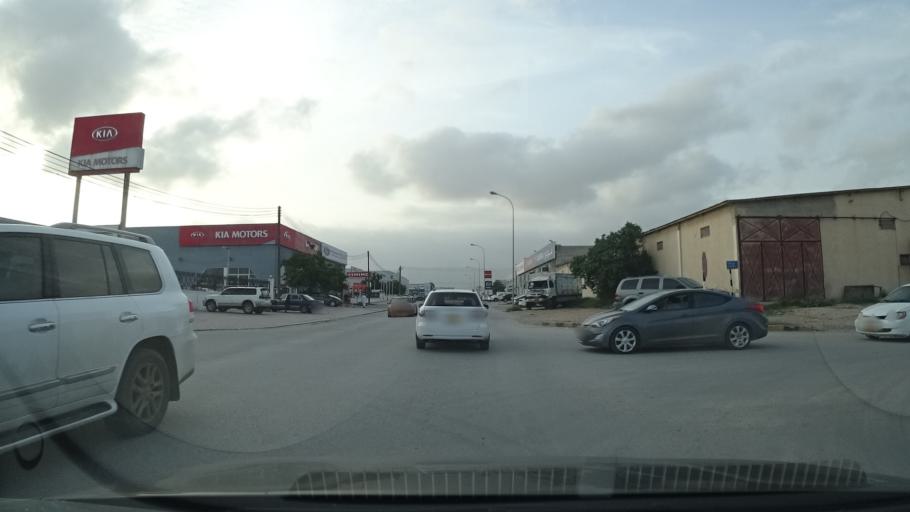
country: OM
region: Zufar
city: Salalah
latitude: 17.0148
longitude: 54.0459
